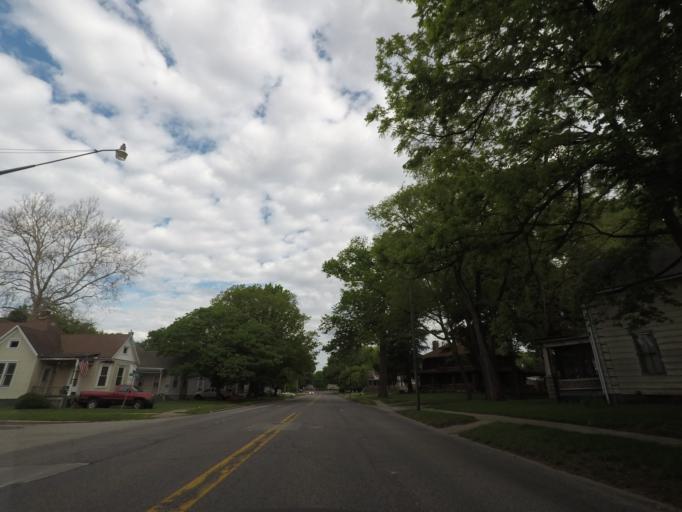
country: US
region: Illinois
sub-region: Logan County
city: Lincoln
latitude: 40.1560
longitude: -89.3637
